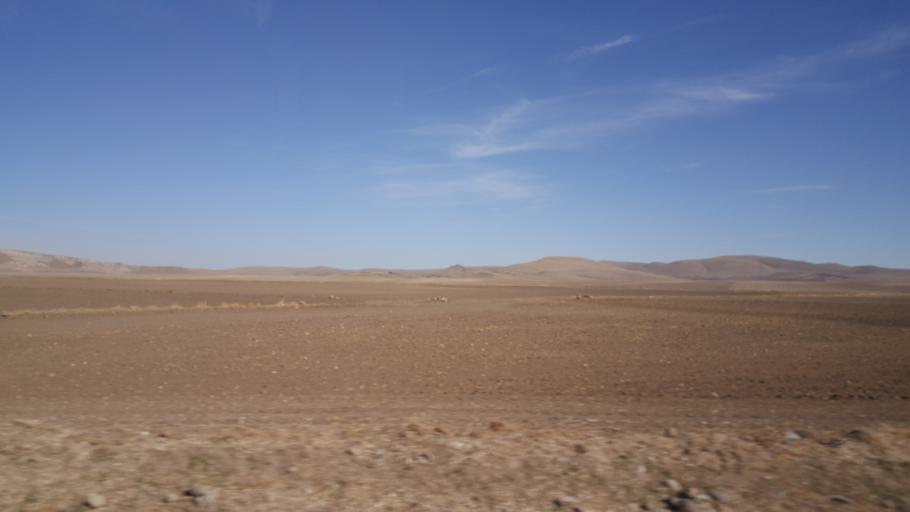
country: TR
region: Ankara
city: Yenice
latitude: 39.3032
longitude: 32.7570
